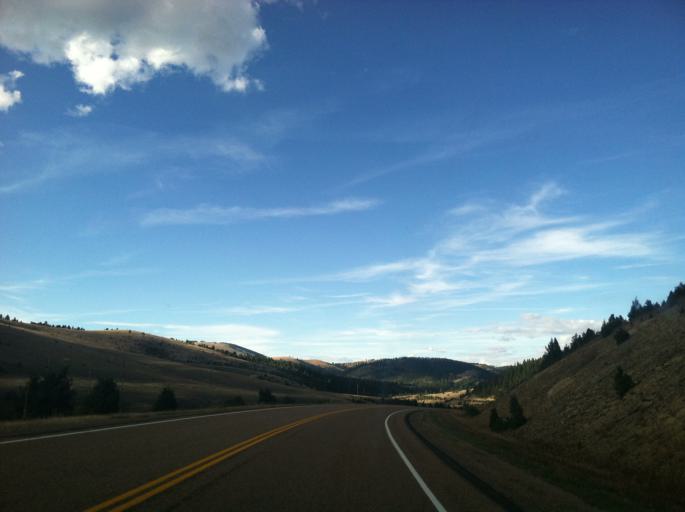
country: US
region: Montana
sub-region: Granite County
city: Philipsburg
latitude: 46.3819
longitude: -113.3128
